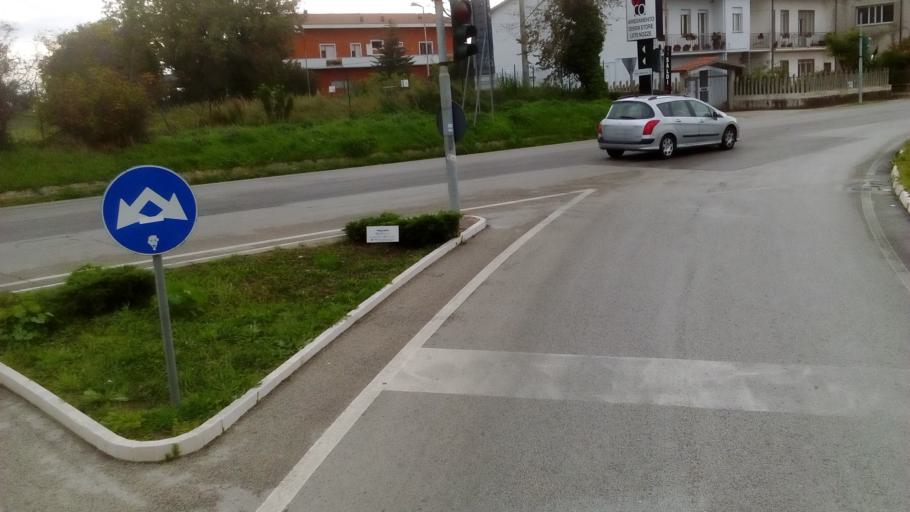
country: IT
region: Abruzzo
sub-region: Provincia di Chieti
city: Vasto
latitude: 42.1010
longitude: 14.7024
